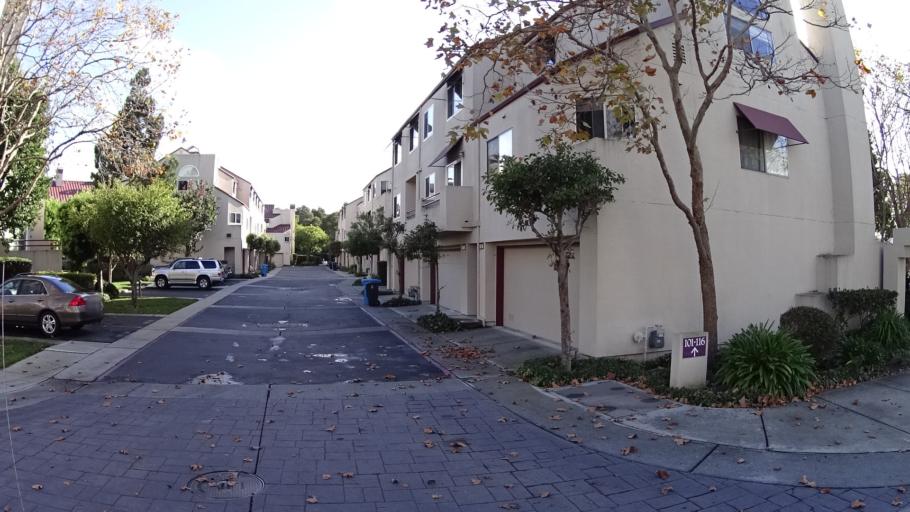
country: US
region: California
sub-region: San Mateo County
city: Foster City
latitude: 37.5564
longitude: -122.2788
